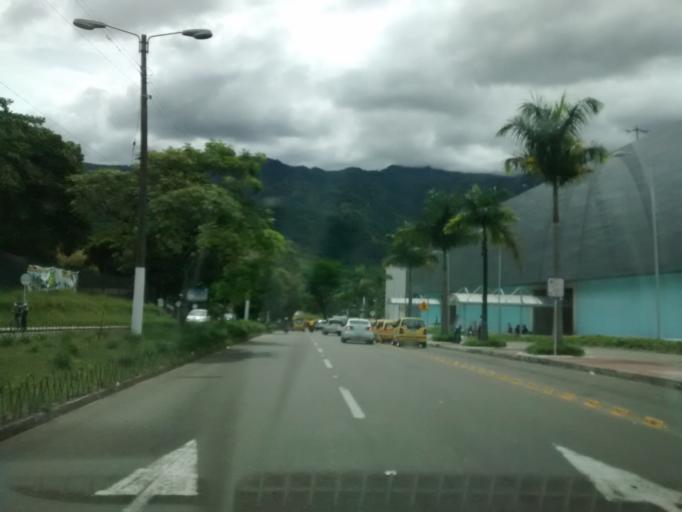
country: CO
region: Tolima
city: Ibague
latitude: 4.4447
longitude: -75.2052
